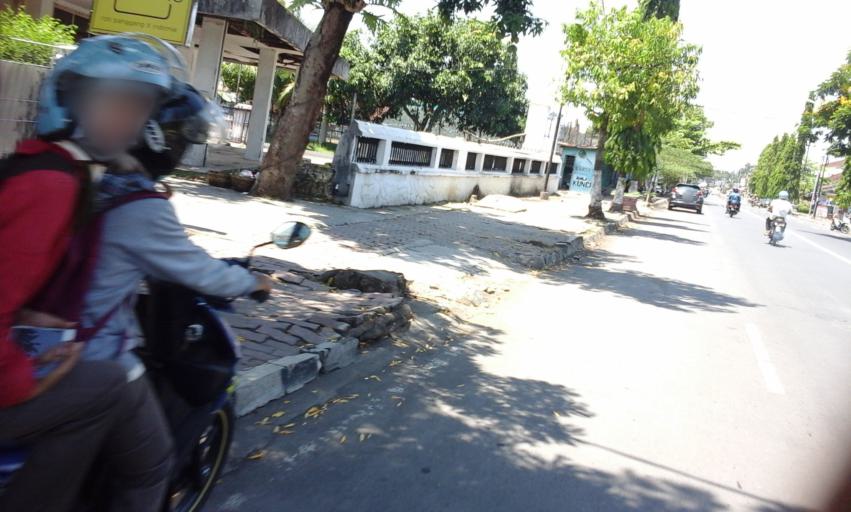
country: ID
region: East Java
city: Krajan
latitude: -8.1642
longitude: 113.7062
